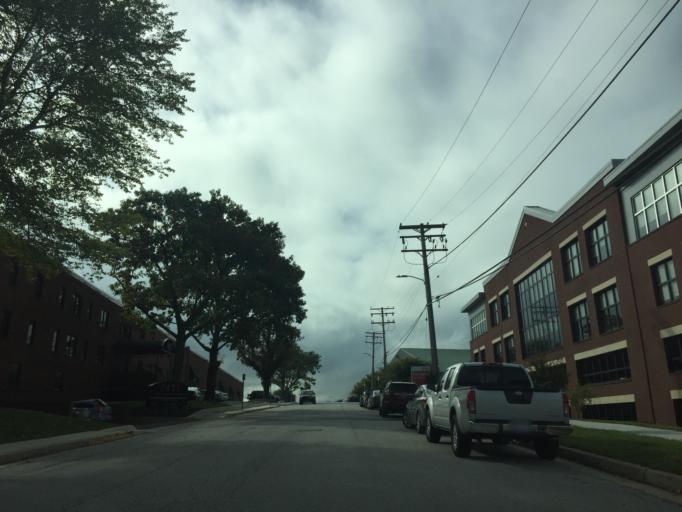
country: US
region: Maryland
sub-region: Baltimore County
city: Lutherville
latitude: 39.3816
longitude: -76.6574
